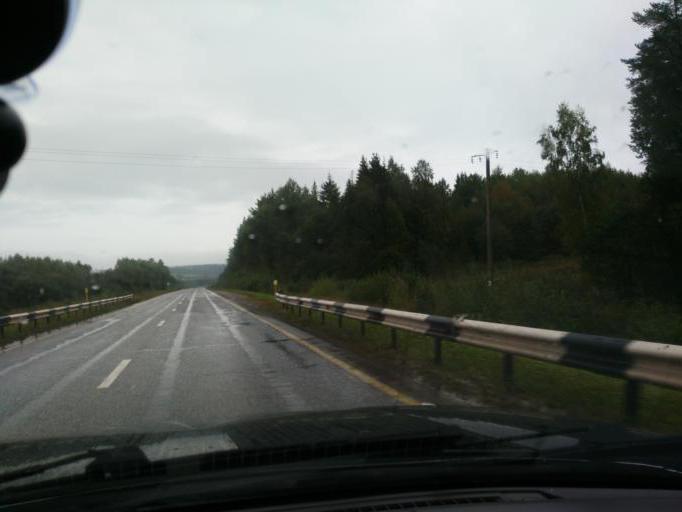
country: RU
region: Perm
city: Osa
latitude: 57.4437
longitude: 55.6399
